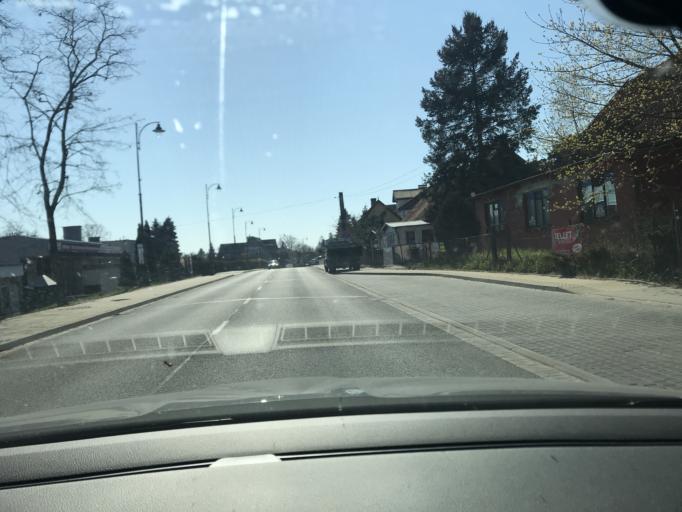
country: PL
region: Pomeranian Voivodeship
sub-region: Powiat nowodworski
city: Krynica Morska
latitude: 54.3745
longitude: 19.4234
